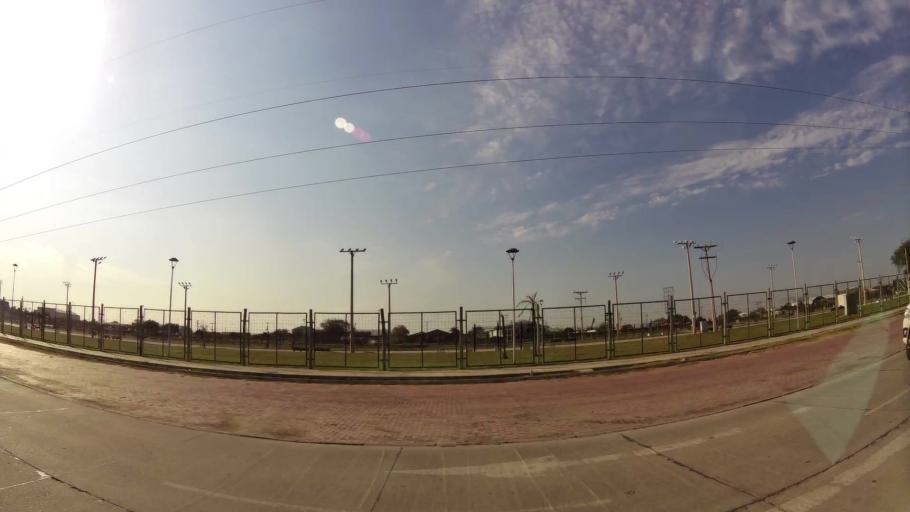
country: BO
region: Santa Cruz
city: Santa Cruz de la Sierra
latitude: -17.7379
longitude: -63.1436
